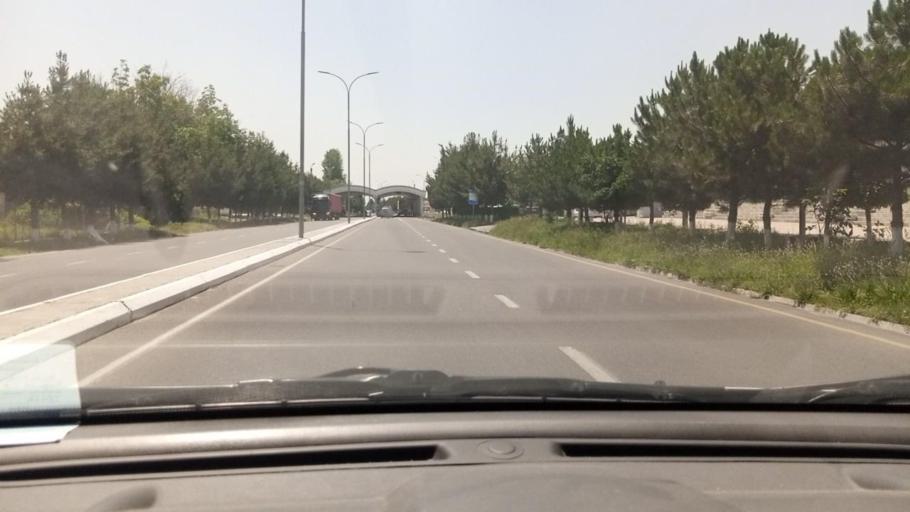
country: UZ
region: Toshkent
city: Urtaowul
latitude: 41.2165
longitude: 69.1737
